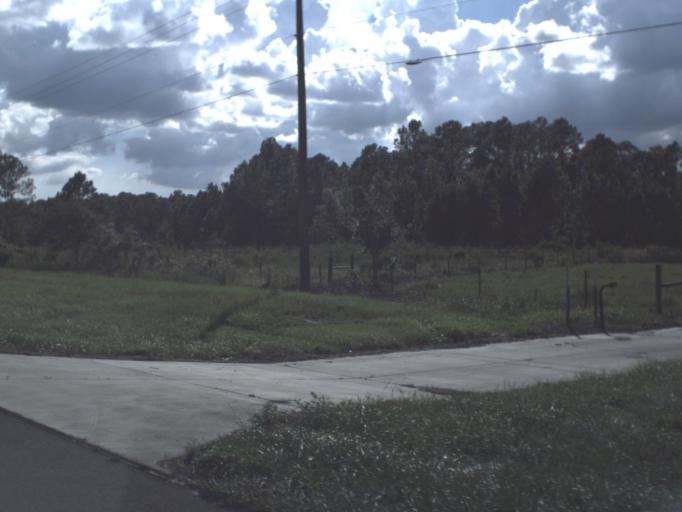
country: US
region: Florida
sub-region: Polk County
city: Polk City
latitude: 28.3409
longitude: -81.8296
